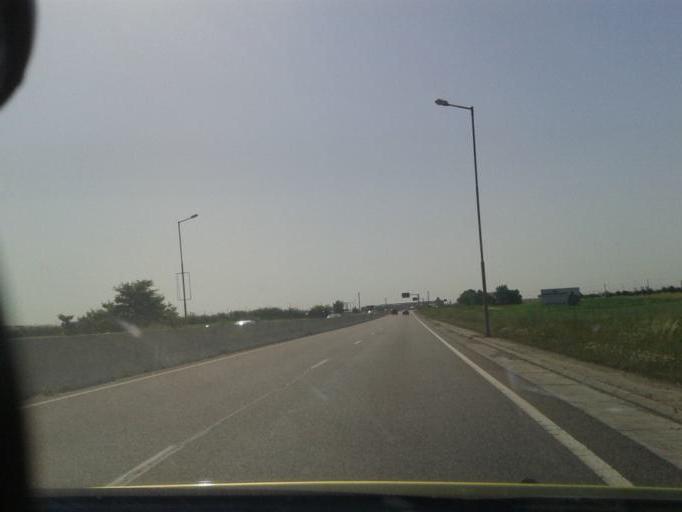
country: RO
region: Prahova
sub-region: Comuna Targsoru Vechi
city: Strejnicu
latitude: 44.9280
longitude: 25.9747
